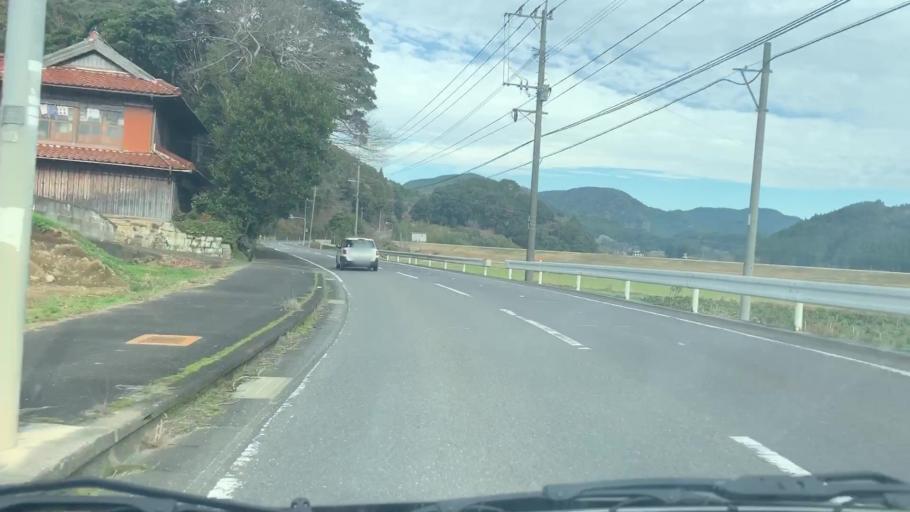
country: JP
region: Saga Prefecture
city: Imaricho-ko
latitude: 33.3153
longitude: 129.9704
